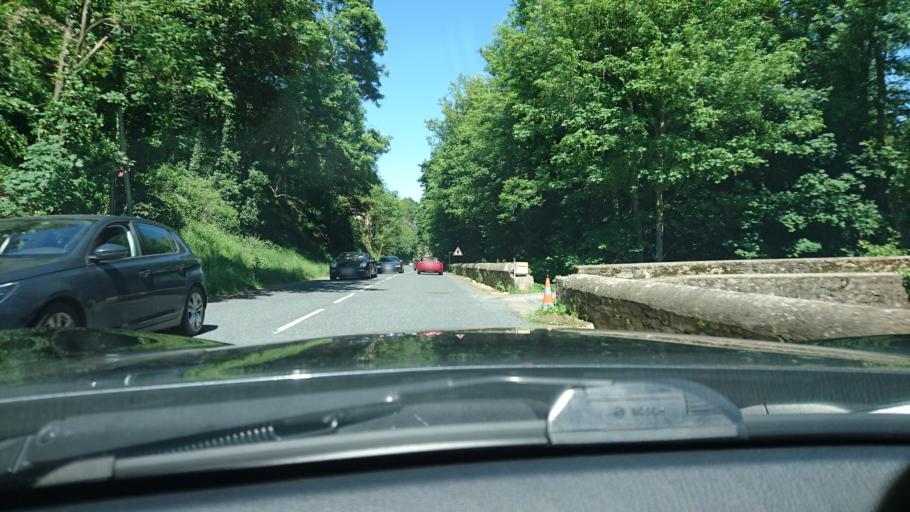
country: FR
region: Rhone-Alpes
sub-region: Departement du Rhone
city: Courzieu
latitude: 45.7089
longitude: 4.5900
